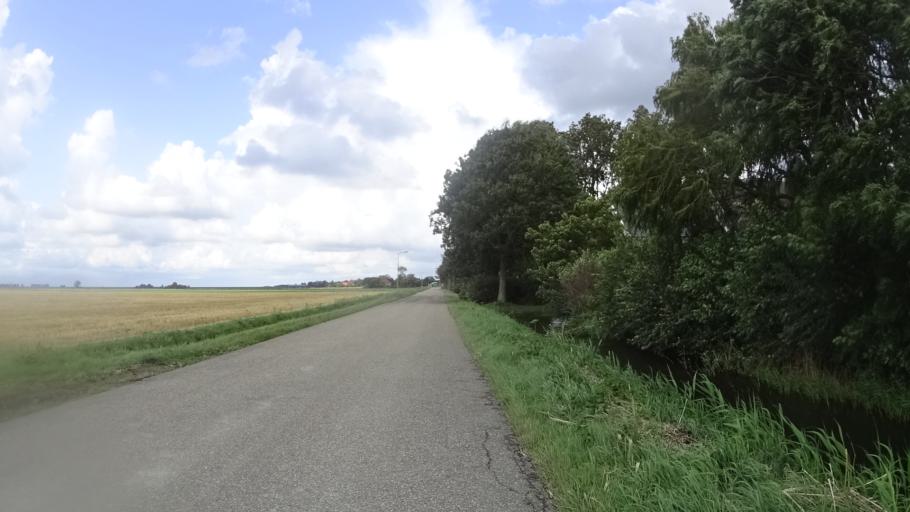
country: NL
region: North Holland
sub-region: Gemeente Schagen
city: Schagen
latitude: 52.8571
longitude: 4.8896
